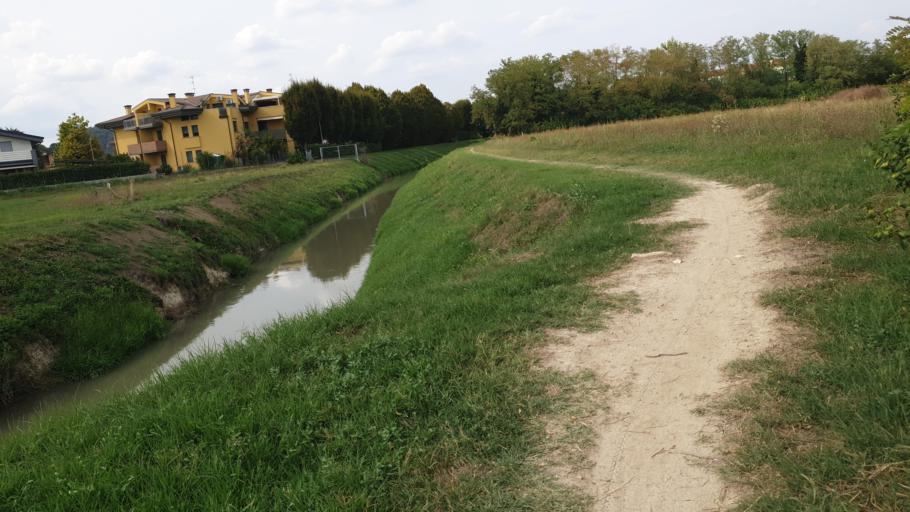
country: IT
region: Veneto
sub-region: Provincia di Padova
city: Montegrotto Terme
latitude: 45.3402
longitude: 11.7781
